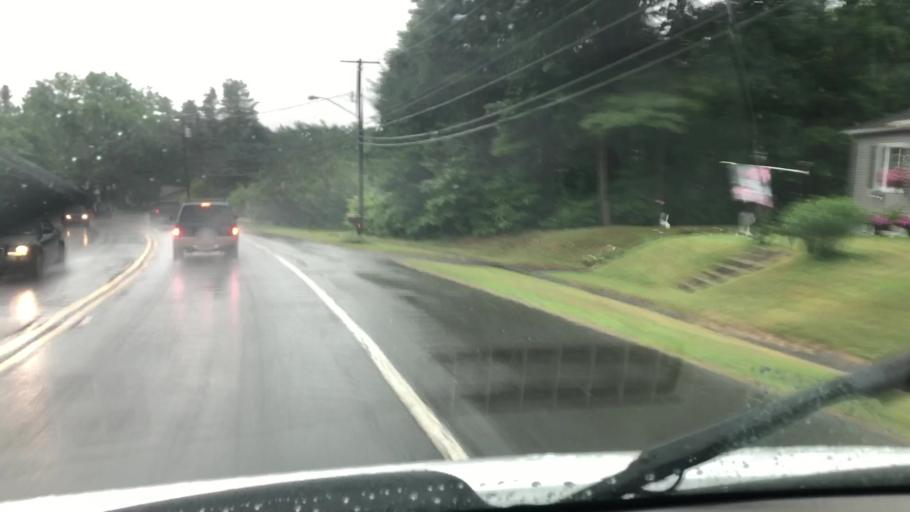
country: US
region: Massachusetts
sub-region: Berkshire County
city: Dalton
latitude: 42.4806
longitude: -73.2048
